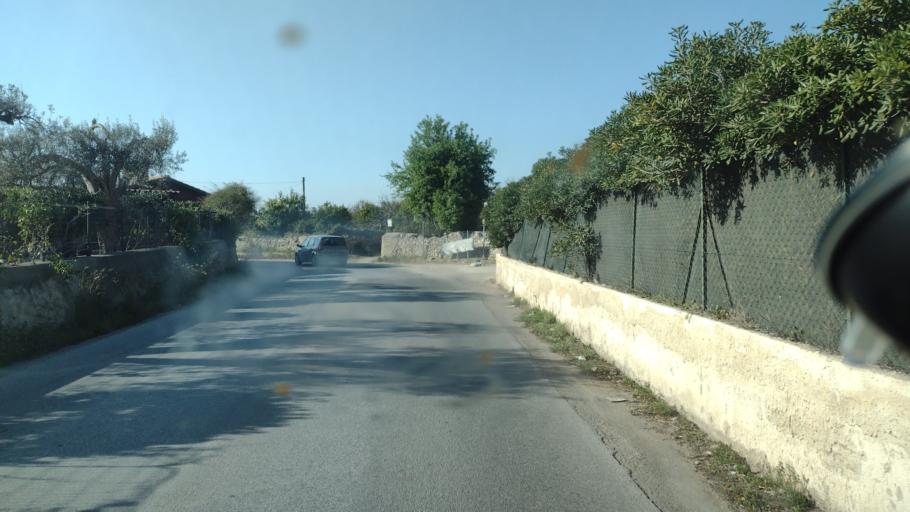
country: IT
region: Sicily
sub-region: Provincia di Siracusa
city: Avola
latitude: 36.8949
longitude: 15.1332
